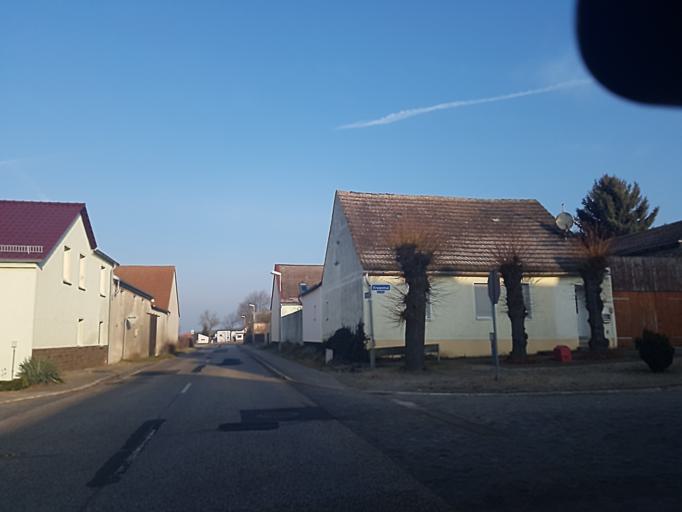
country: DE
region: Brandenburg
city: Bruck
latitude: 52.2289
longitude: 12.7149
